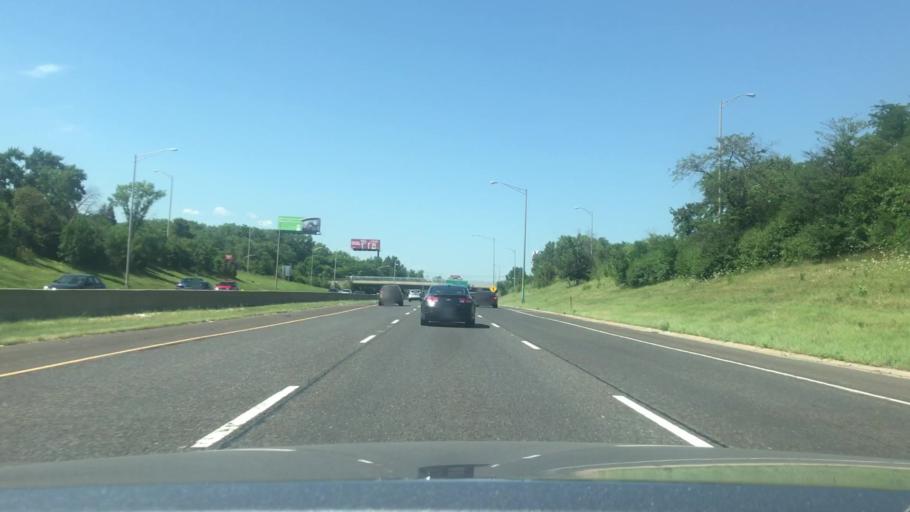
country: US
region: Illinois
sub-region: Cook County
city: Calumet Park
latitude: 41.6633
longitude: -87.6626
